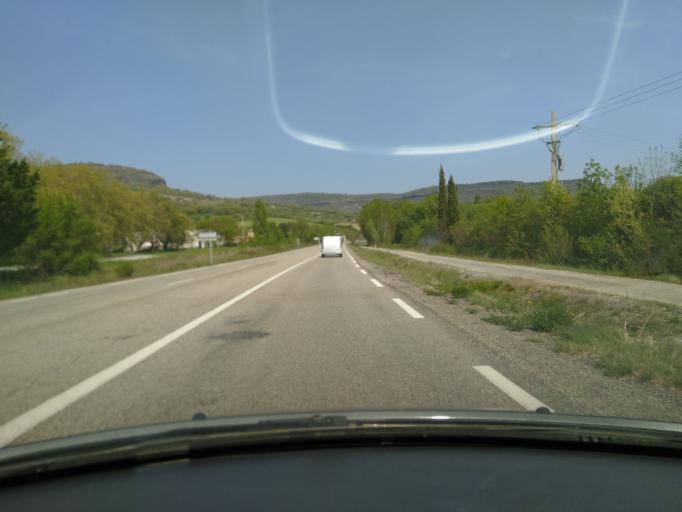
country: FR
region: Rhone-Alpes
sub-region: Departement de l'Ardeche
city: Villeneuve-de-Berg
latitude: 44.5885
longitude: 4.5368
